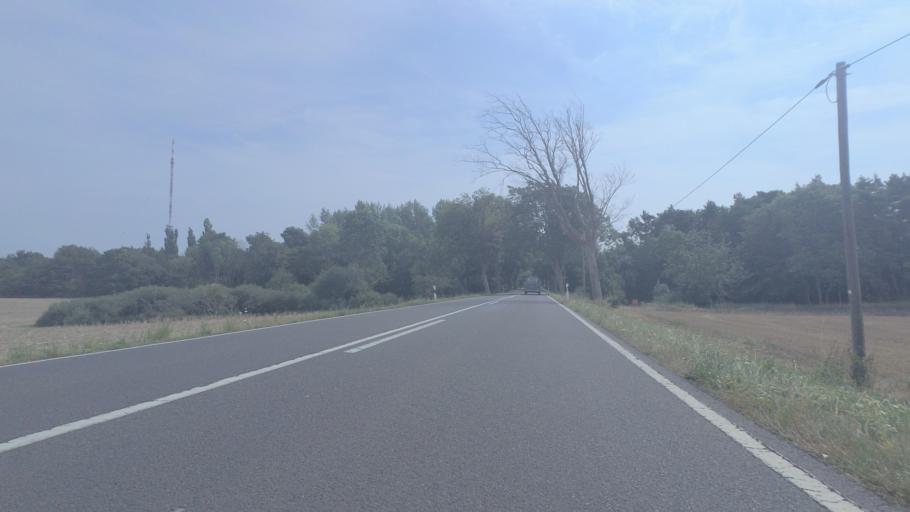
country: DE
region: Mecklenburg-Vorpommern
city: Garz
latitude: 54.3246
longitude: 13.3323
